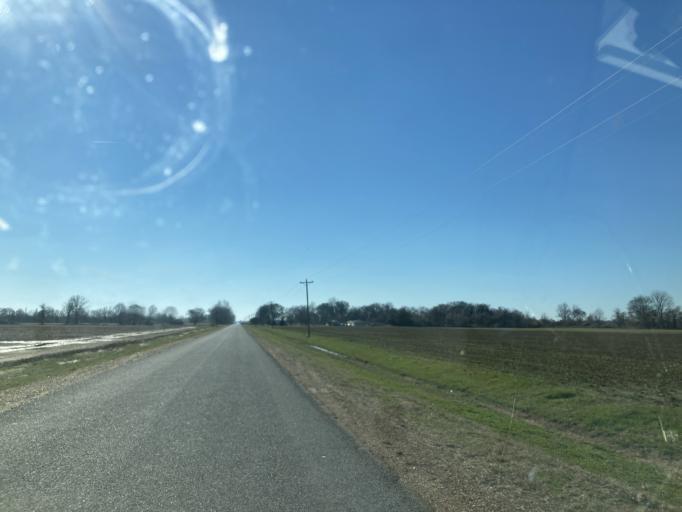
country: US
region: Mississippi
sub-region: Yazoo County
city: Yazoo City
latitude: 32.9733
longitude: -90.5946
